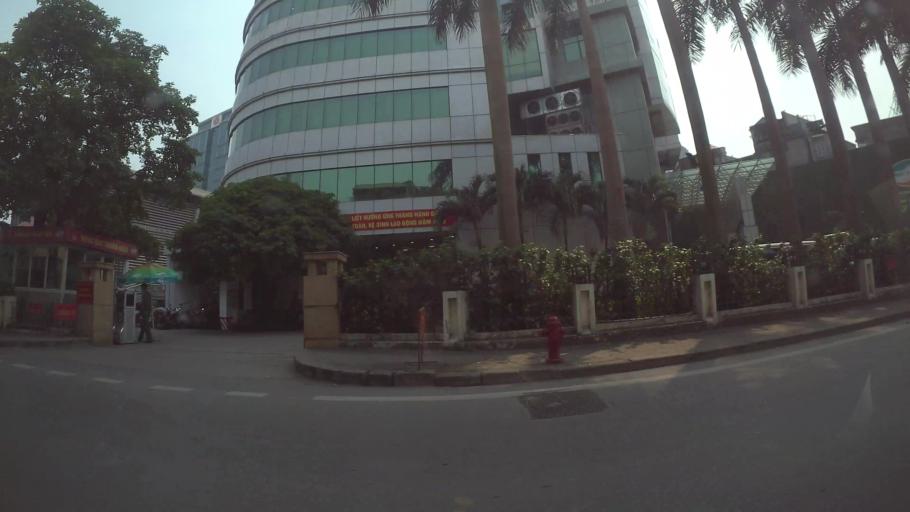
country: VN
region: Ha Noi
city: Dong Da
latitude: 21.0301
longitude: 105.8270
